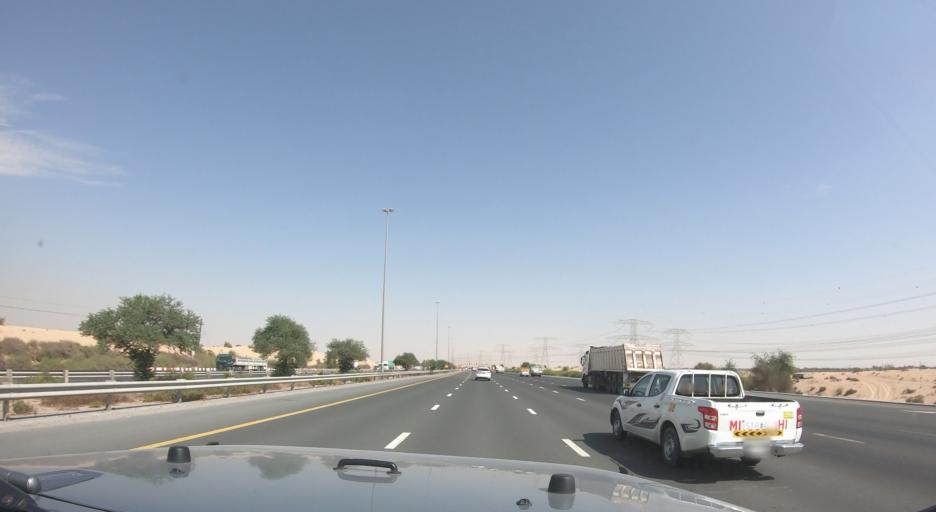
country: AE
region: Ash Shariqah
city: Sharjah
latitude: 25.1694
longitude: 55.5036
